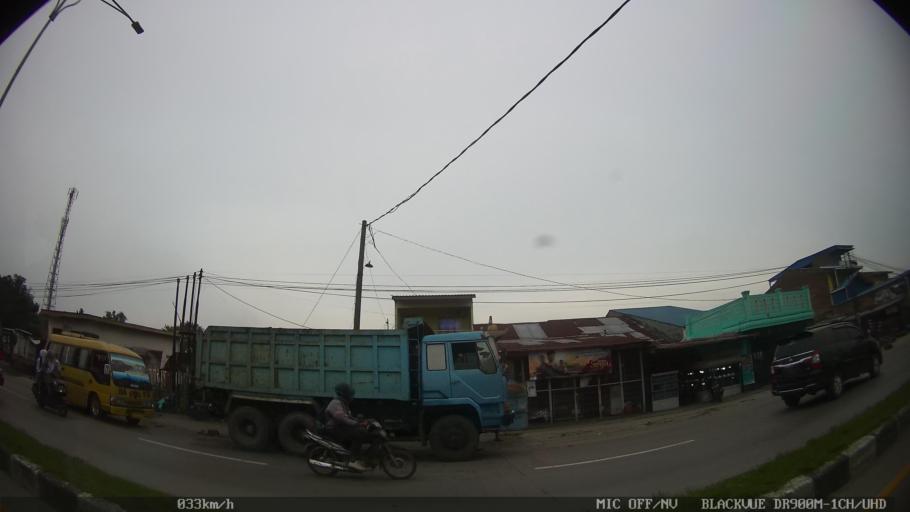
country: ID
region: North Sumatra
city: Deli Tua
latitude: 3.5326
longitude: 98.7296
